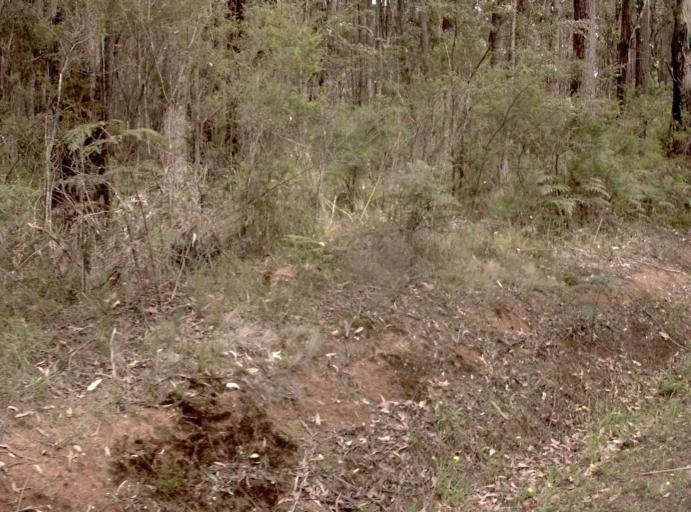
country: AU
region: Victoria
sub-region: Latrobe
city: Traralgon
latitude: -38.0020
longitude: 146.4137
